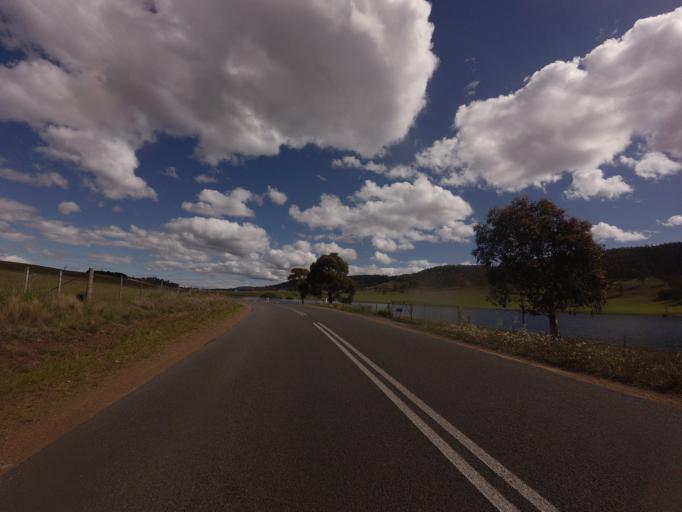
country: AU
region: Tasmania
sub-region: Brighton
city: Bridgewater
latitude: -42.4174
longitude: 147.3110
